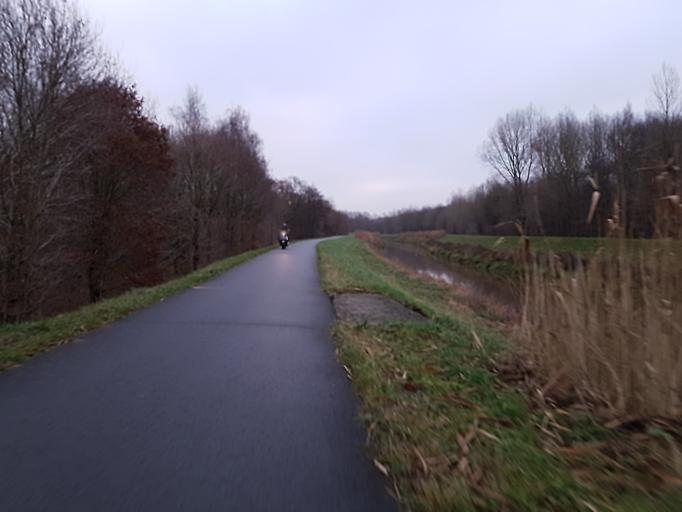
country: BE
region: Flanders
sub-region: Provincie Vlaams-Brabant
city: Rotselaar
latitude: 50.9723
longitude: 4.7354
